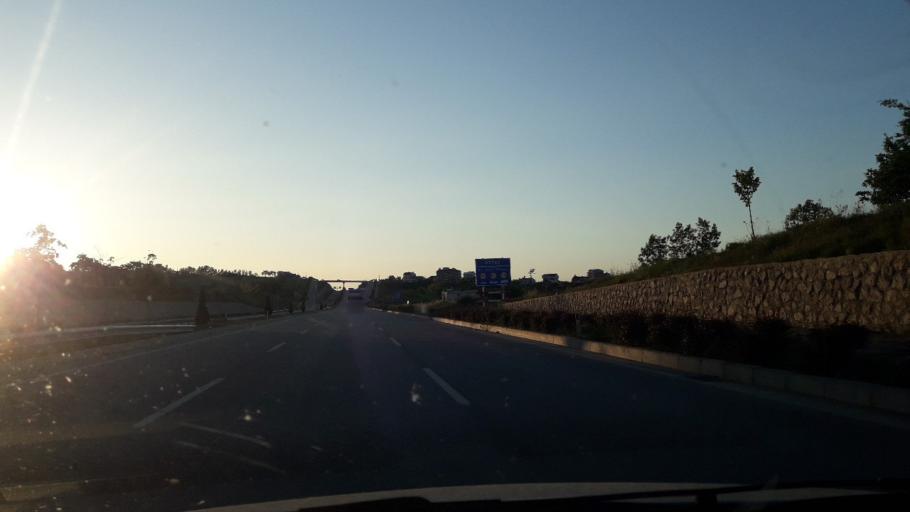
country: TR
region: Sinop
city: Gerze
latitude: 41.7961
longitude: 35.1848
